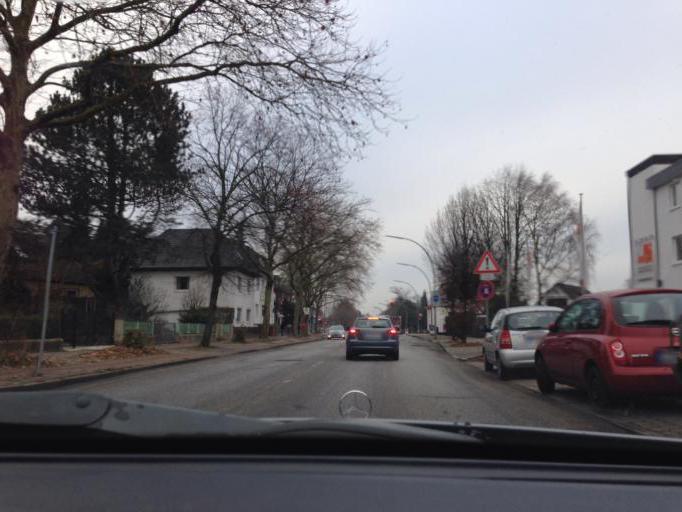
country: DE
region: Hamburg
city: Farmsen-Berne
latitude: 53.6003
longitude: 10.1412
